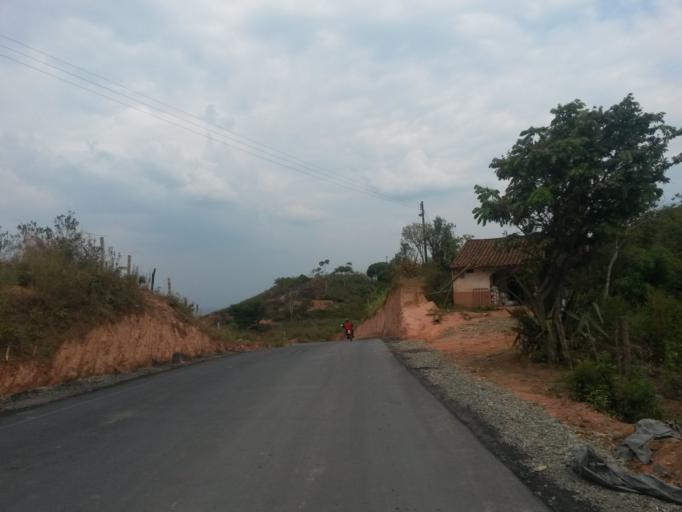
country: CO
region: Cauca
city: Buenos Aires
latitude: 3.0532
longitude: -76.6340
